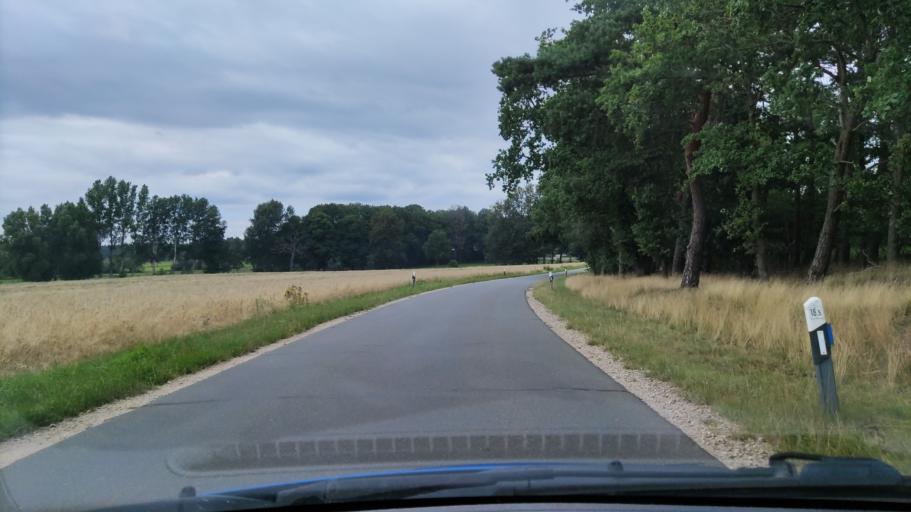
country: DE
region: Lower Saxony
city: Weste
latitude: 53.0257
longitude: 10.7282
